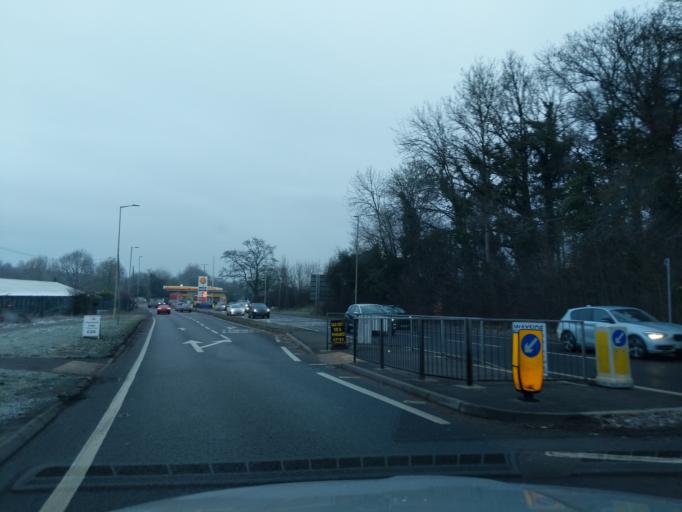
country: GB
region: England
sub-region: Hertfordshire
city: Abbots Langley
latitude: 51.6861
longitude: -0.4316
